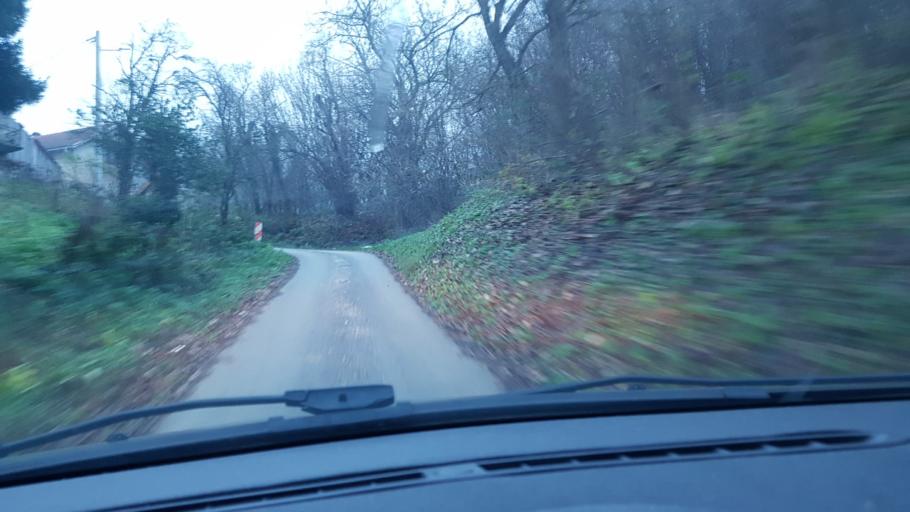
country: HR
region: Krapinsko-Zagorska
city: Pregrada
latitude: 46.2044
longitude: 15.7873
